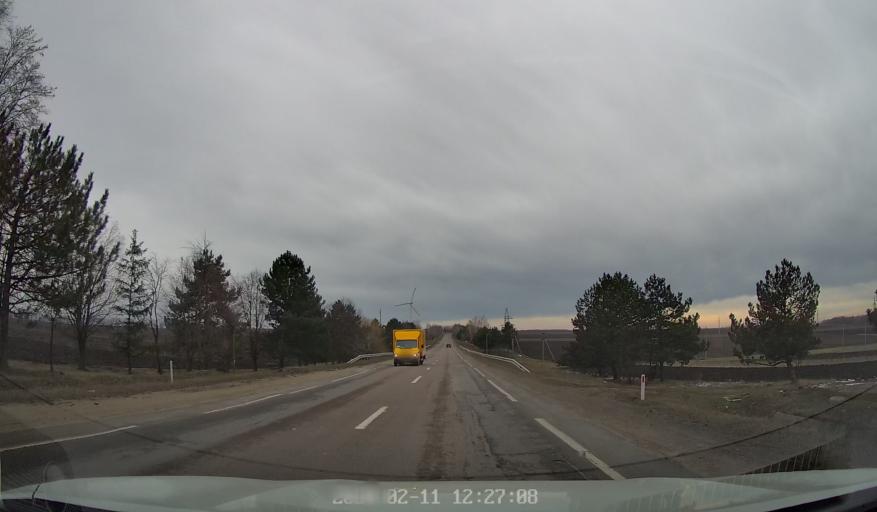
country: MD
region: Raionul Edinet
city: Edinet
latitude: 48.1518
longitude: 27.3202
